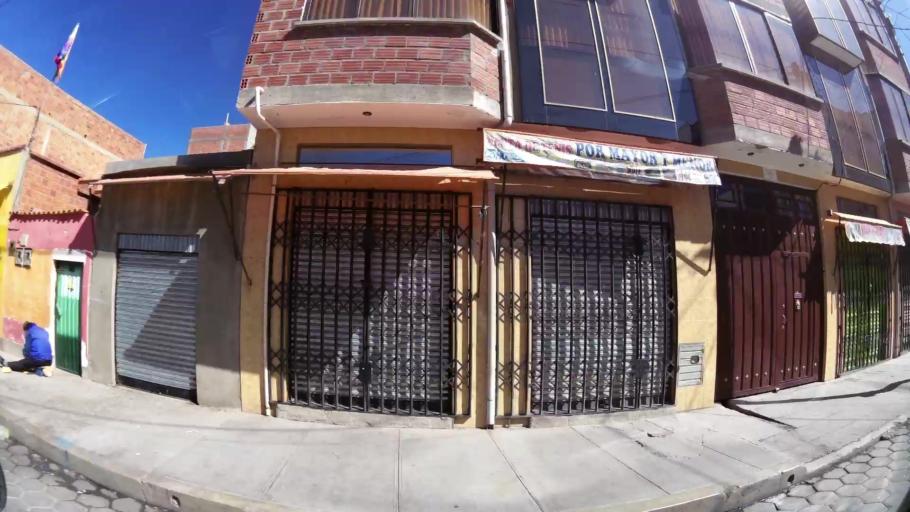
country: BO
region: La Paz
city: La Paz
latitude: -16.5146
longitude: -68.1626
